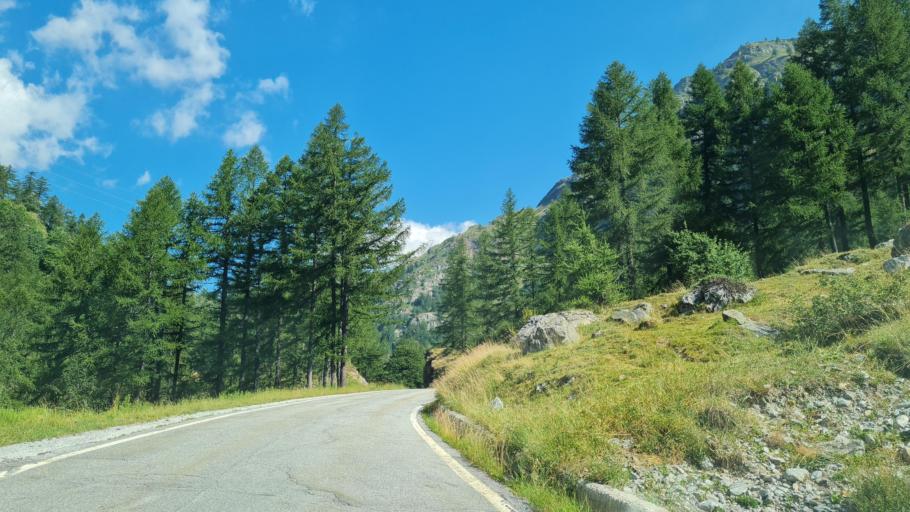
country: IT
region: Piedmont
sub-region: Provincia Verbano-Cusio-Ossola
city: Formazza
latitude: 46.3981
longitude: 8.4203
